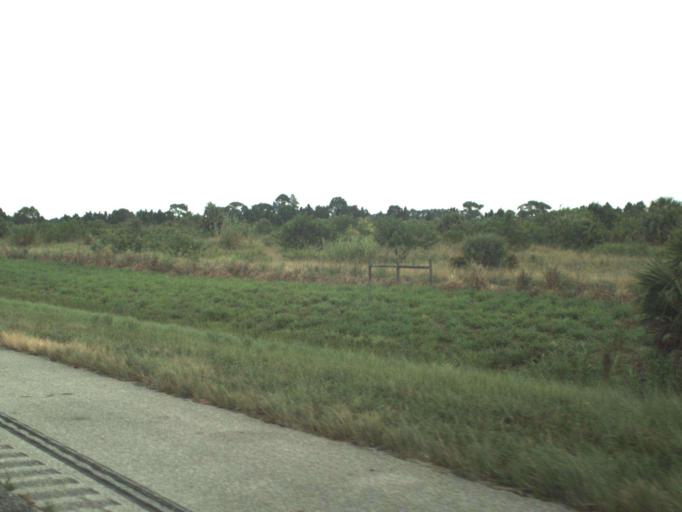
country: US
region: Florida
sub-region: Palm Beach County
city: Tequesta
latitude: 26.9831
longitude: -80.1850
